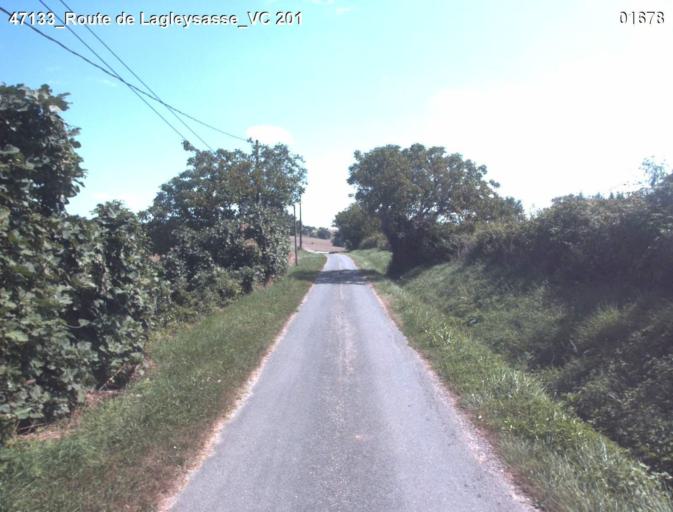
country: FR
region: Aquitaine
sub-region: Departement du Lot-et-Garonne
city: Laplume
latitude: 44.0591
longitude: 0.5392
